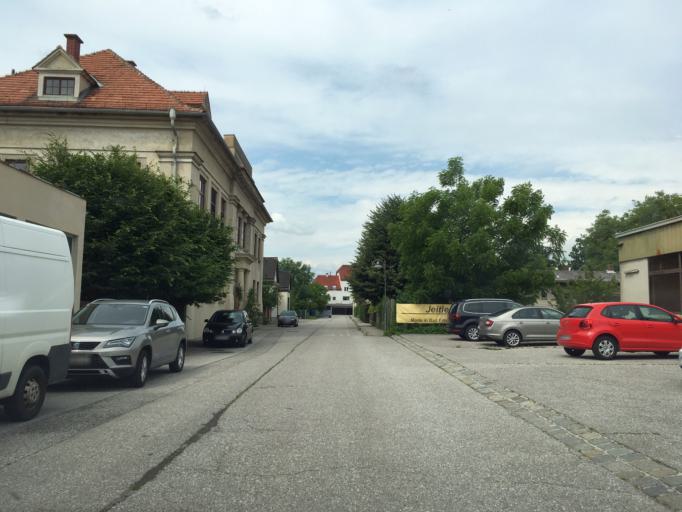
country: AT
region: Lower Austria
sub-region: Politischer Bezirk Wiener Neustadt
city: Bad Erlach
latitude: 47.7283
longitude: 16.2177
